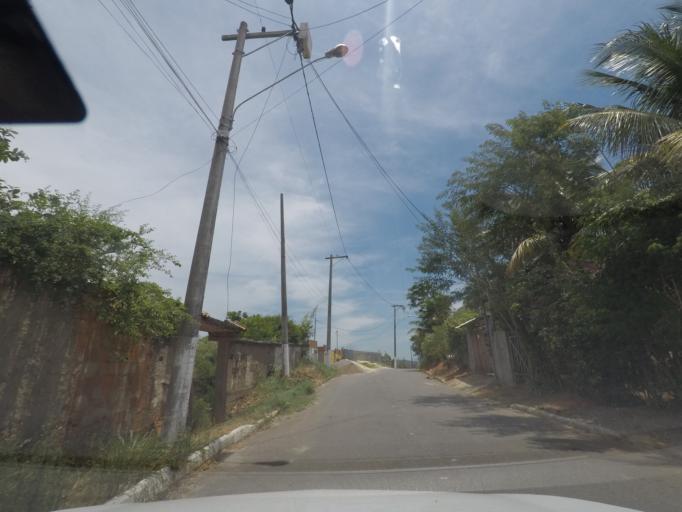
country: BR
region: Rio de Janeiro
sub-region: Marica
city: Marica
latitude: -22.9322
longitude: -42.8263
